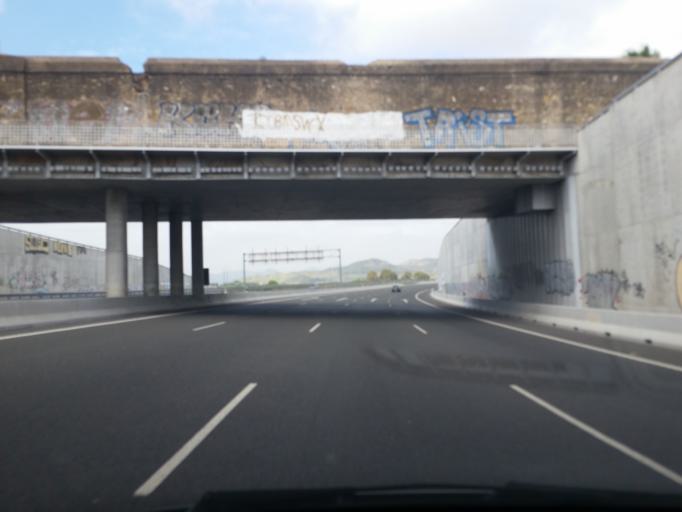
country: ES
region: Andalusia
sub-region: Provincia de Malaga
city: Alhaurin de la Torre
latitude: 36.6871
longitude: -4.5269
